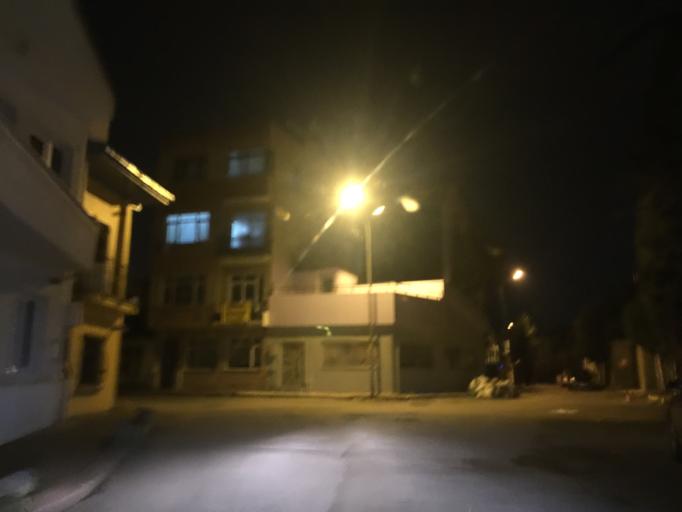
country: TR
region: Istanbul
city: Icmeler
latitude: 40.8151
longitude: 29.3062
